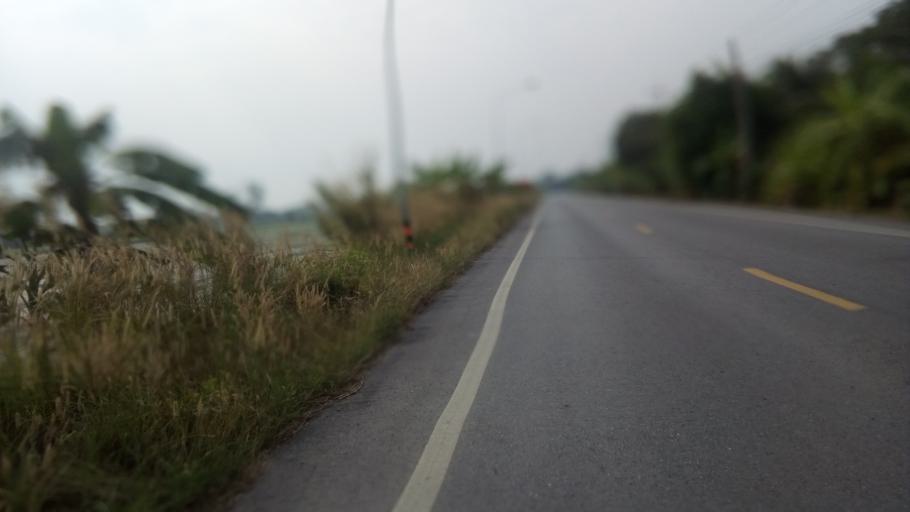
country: TH
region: Pathum Thani
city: Ban Rangsit
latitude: 14.0400
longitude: 100.8245
